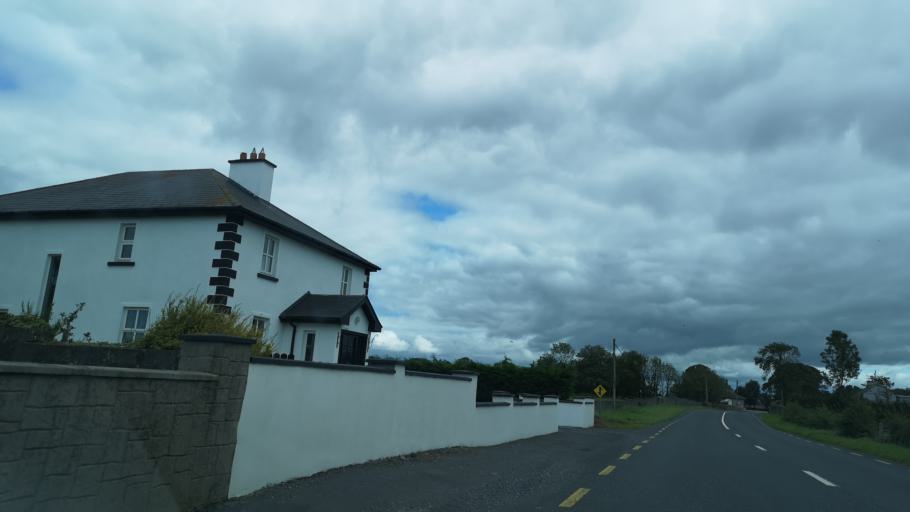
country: IE
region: Connaught
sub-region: County Galway
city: Ballinasloe
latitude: 53.2999
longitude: -8.1232
